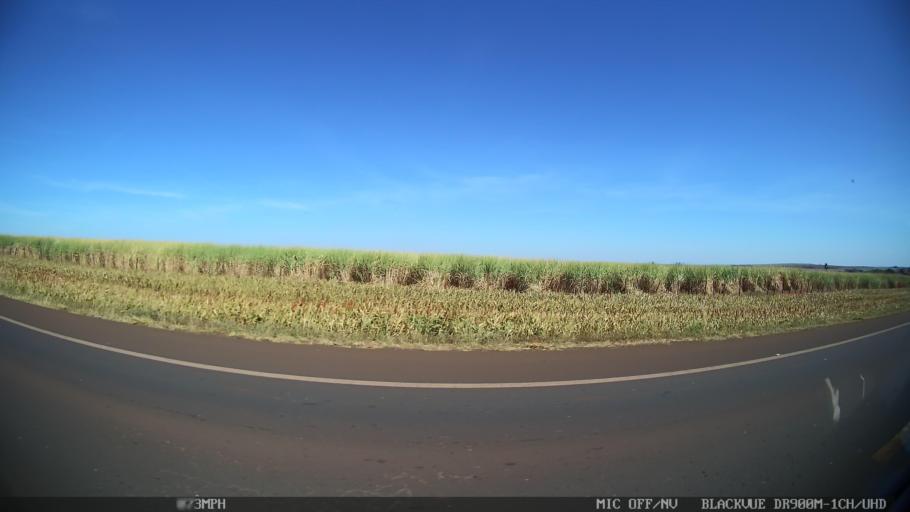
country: BR
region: Sao Paulo
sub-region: Ipua
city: Ipua
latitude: -20.4610
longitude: -48.1424
